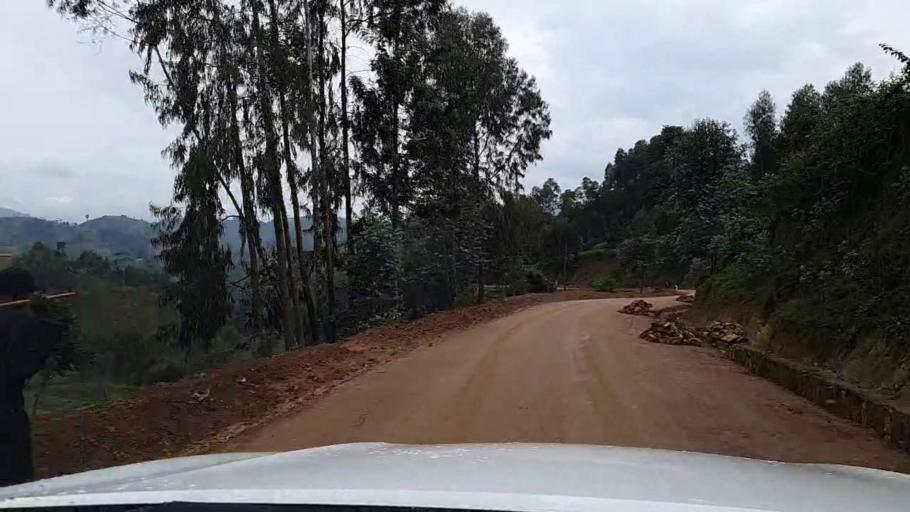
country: RW
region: Southern Province
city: Nzega
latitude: -2.4597
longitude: 29.4665
